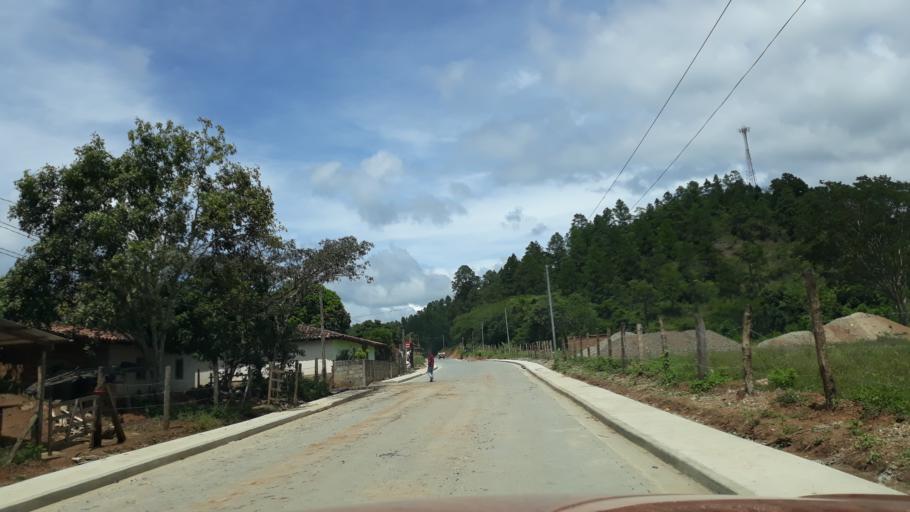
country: HN
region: El Paraiso
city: Santa Cruz
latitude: 13.7352
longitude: -86.6245
